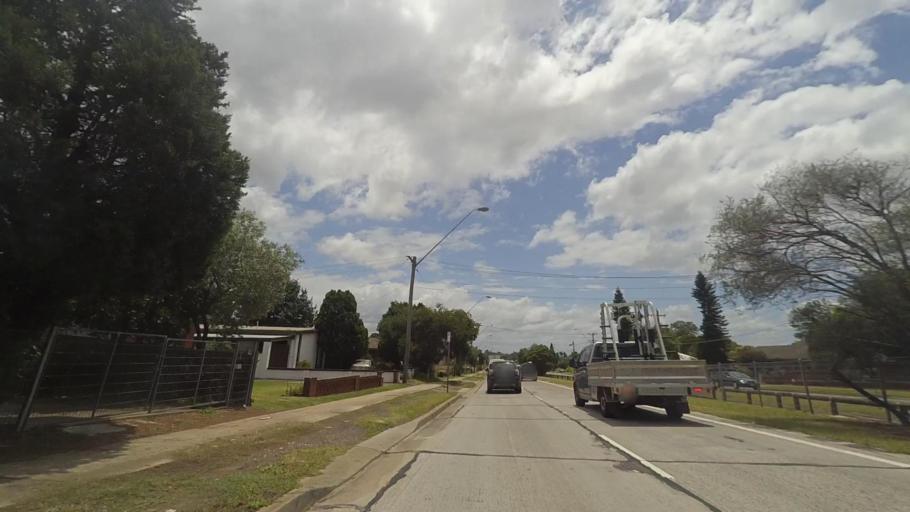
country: AU
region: New South Wales
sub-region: Fairfield
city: Cabramatta West
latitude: -33.8958
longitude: 150.9218
